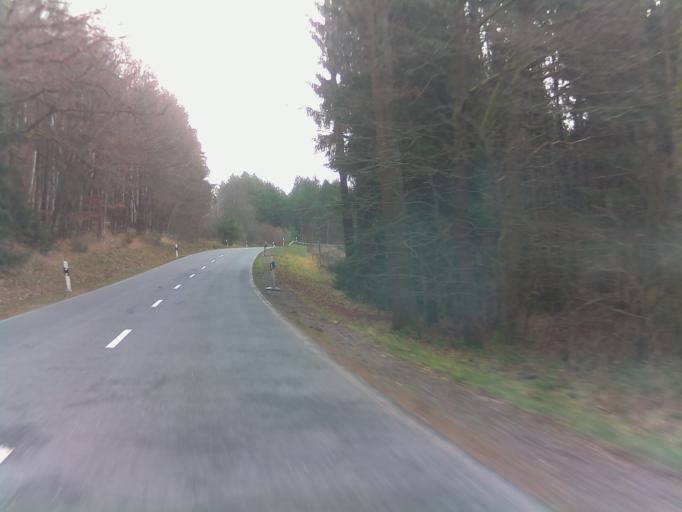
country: DE
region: Thuringia
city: Tautendorf
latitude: 50.8097
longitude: 11.8889
